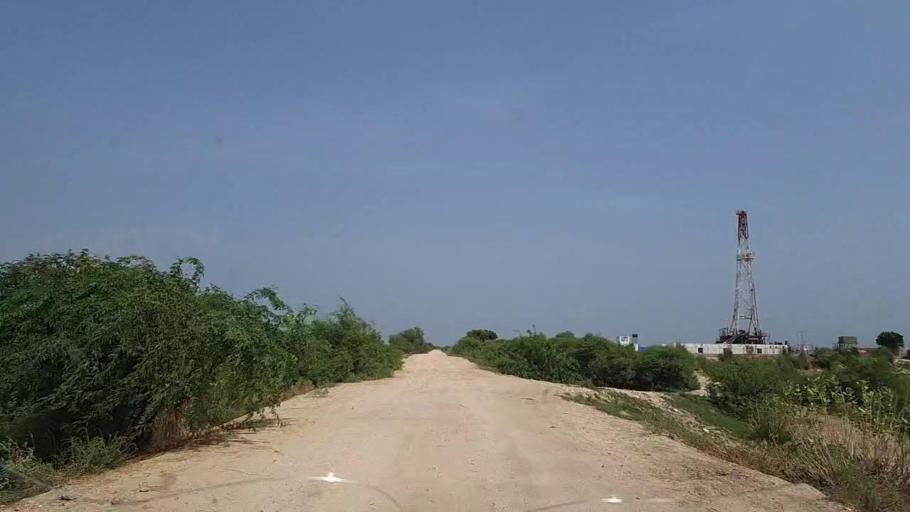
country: PK
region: Sindh
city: Ghotki
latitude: 28.1161
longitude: 69.3844
